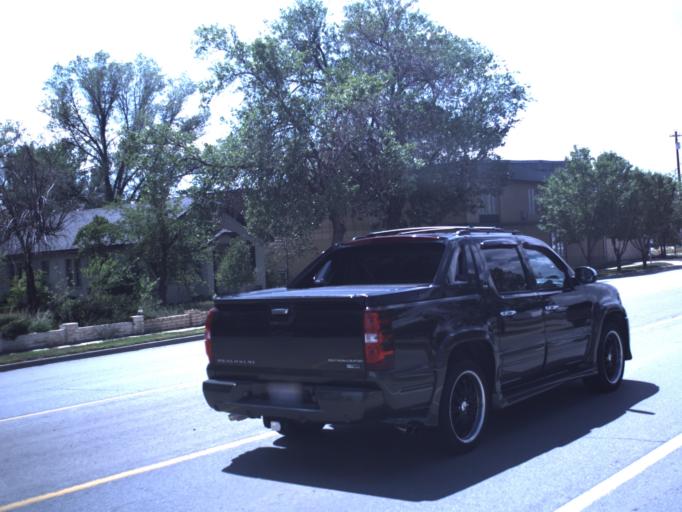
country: US
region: Utah
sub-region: Duchesne County
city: Duchesne
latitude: 40.1635
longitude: -110.3970
